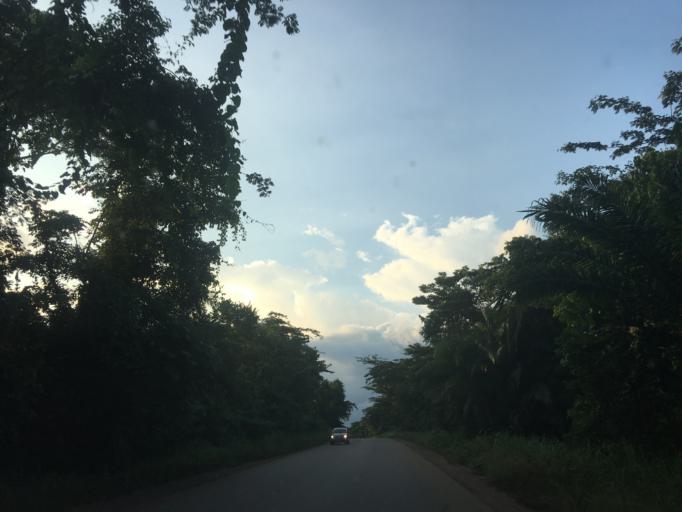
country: GH
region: Western
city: Bibiani
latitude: 6.6736
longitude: -2.4348
